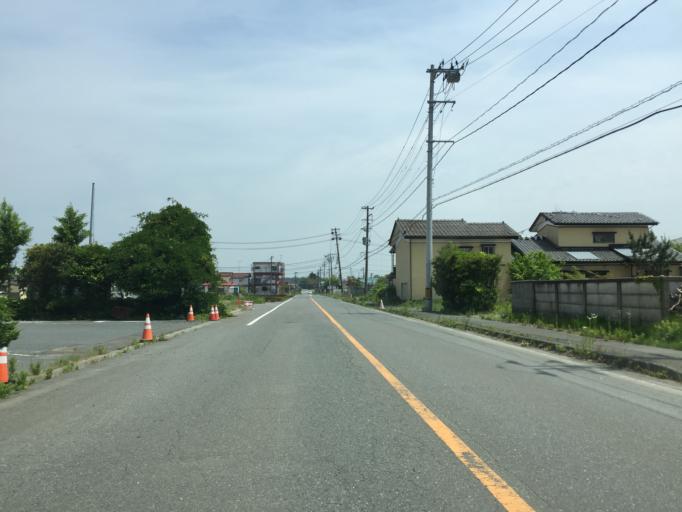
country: JP
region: Fukushima
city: Namie
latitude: 37.4890
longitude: 140.9935
